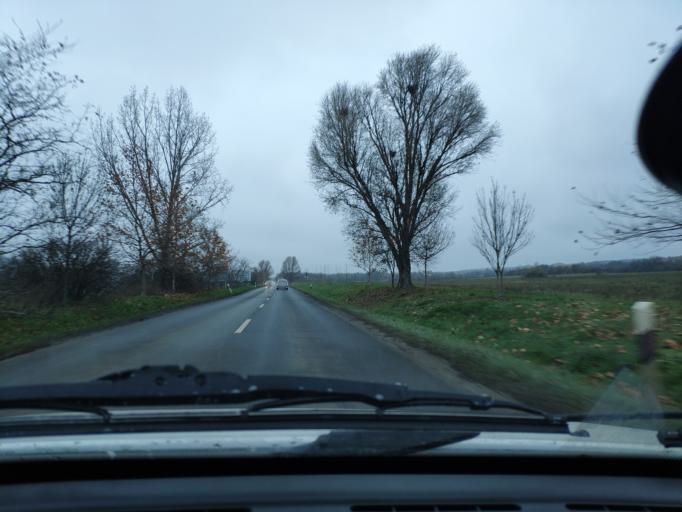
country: HU
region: Pest
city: Tarnok
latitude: 47.3941
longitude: 18.8467
